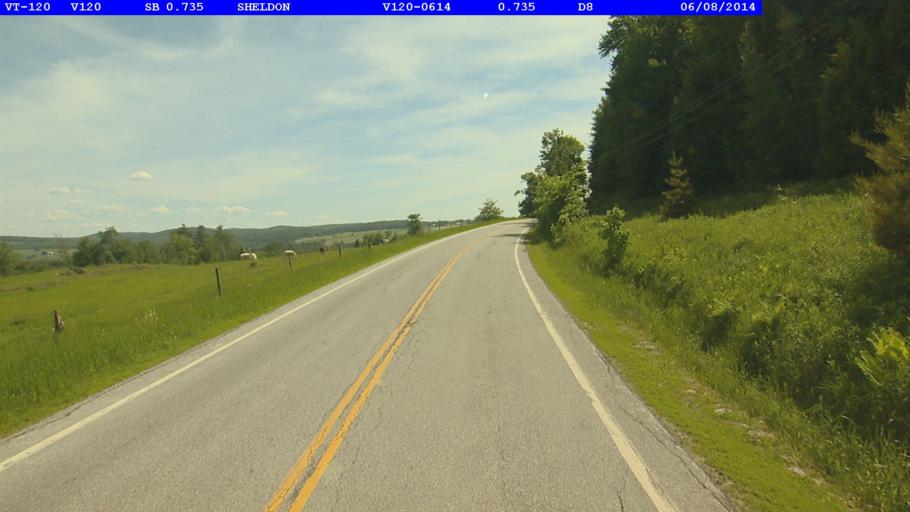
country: US
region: Vermont
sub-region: Franklin County
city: Enosburg Falls
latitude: 44.9206
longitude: -72.9017
